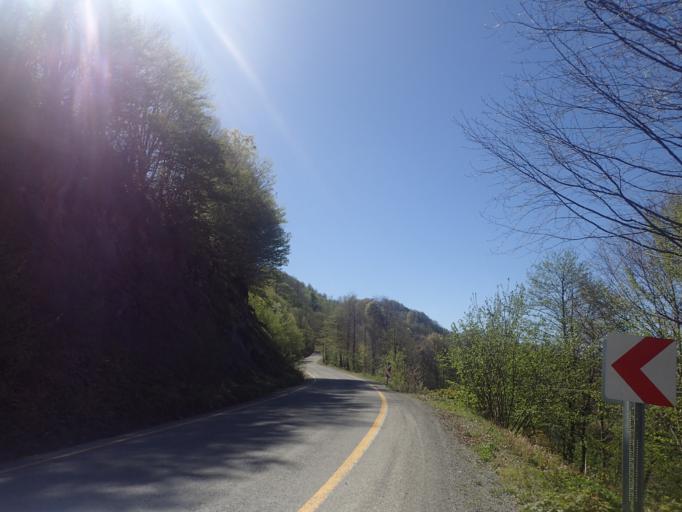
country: TR
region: Ordu
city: Kabaduz
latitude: 40.8149
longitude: 37.9063
